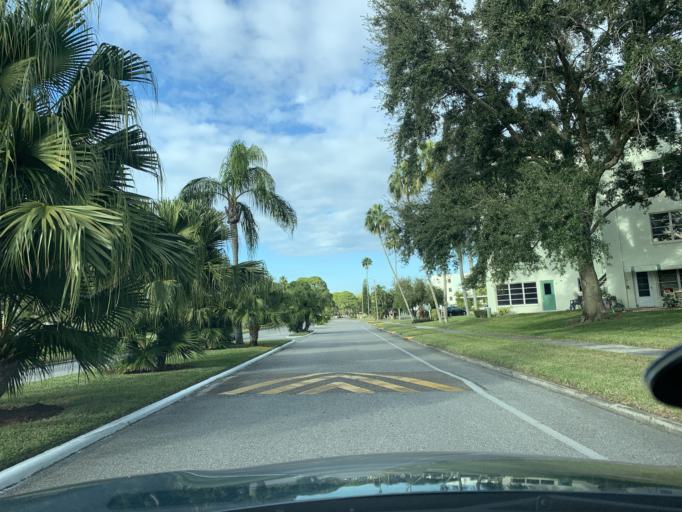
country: US
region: Florida
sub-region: Pinellas County
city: Bay Pines
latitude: 27.8240
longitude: -82.7497
